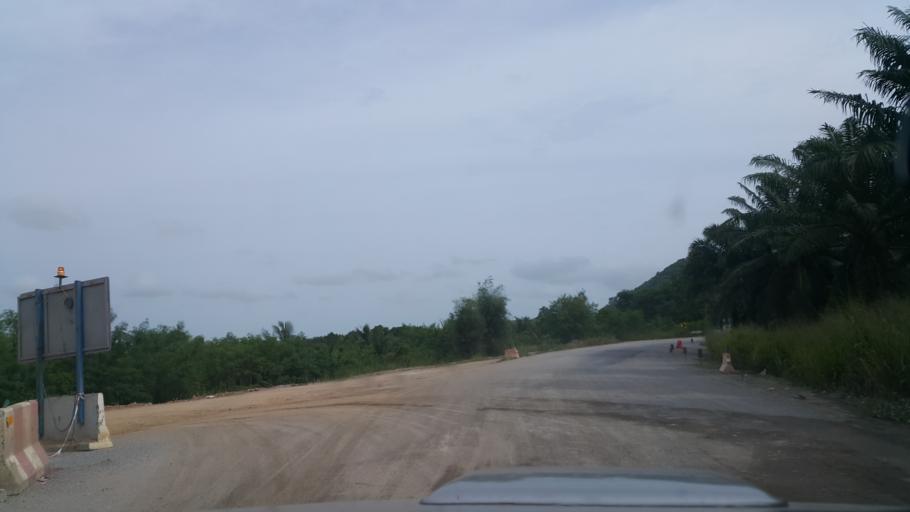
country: TH
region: Rayong
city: Ban Chang
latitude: 12.7664
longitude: 100.9936
